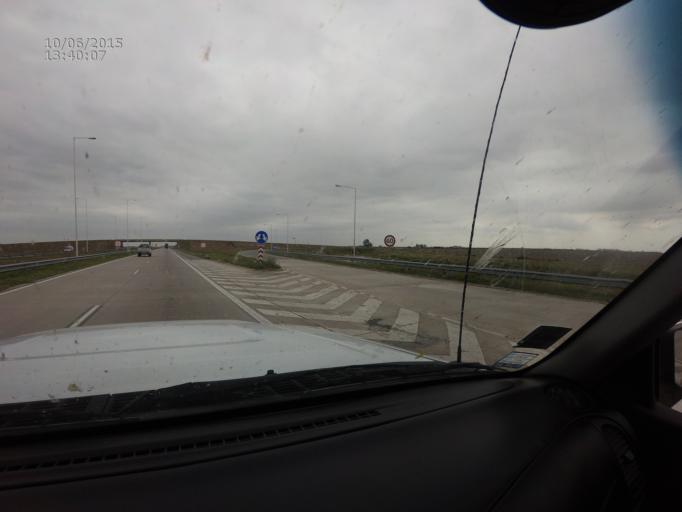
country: AR
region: Cordoba
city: Leones
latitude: -32.5975
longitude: -62.4712
